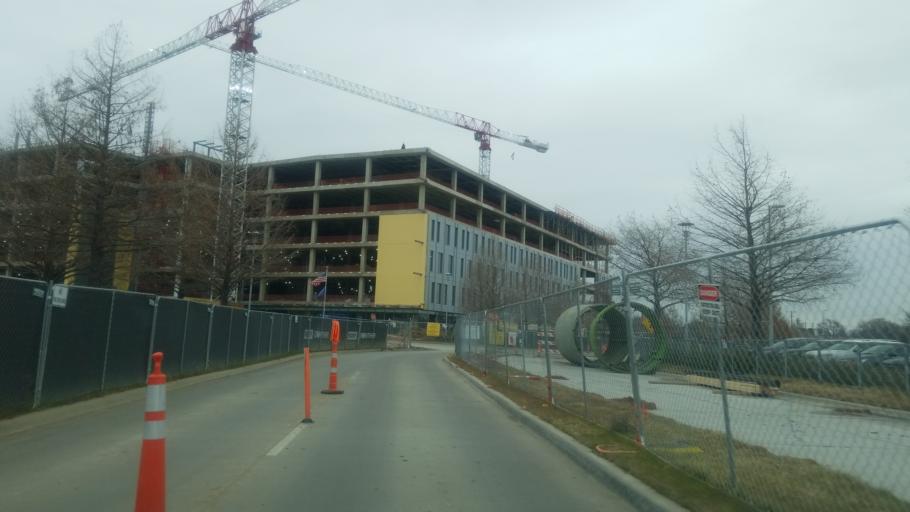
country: US
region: Texas
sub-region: Dallas County
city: Dallas
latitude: 32.8138
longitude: -96.8325
